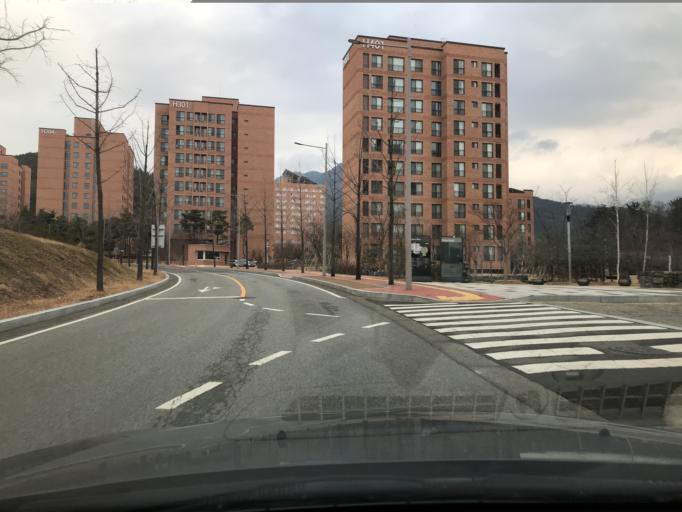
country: KR
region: Daegu
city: Hwawon
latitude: 35.7017
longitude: 128.4603
